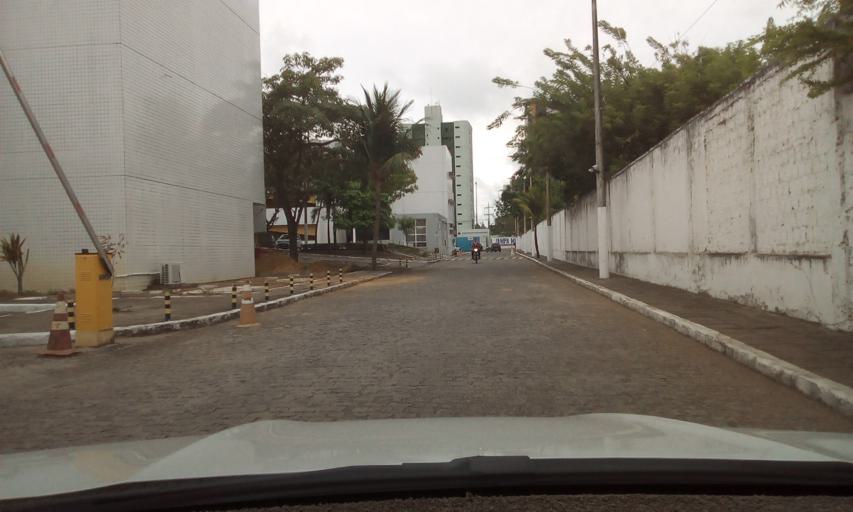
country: BR
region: Paraiba
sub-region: Joao Pessoa
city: Joao Pessoa
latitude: -7.0951
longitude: -34.8496
